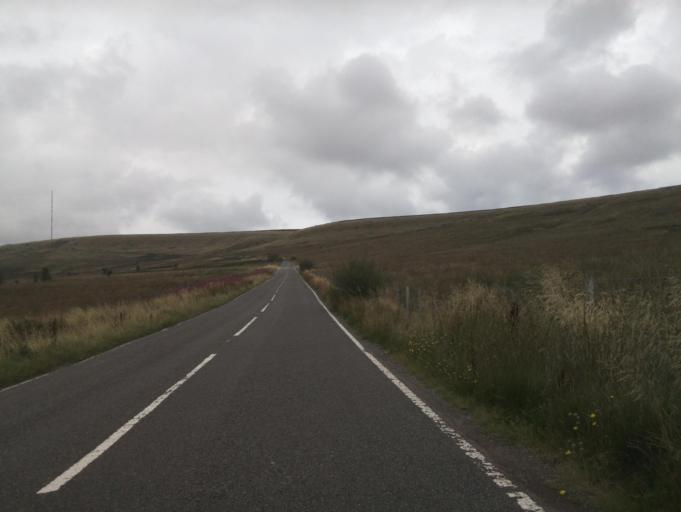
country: GB
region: England
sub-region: Kirklees
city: Meltham
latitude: 53.5151
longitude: -1.8523
